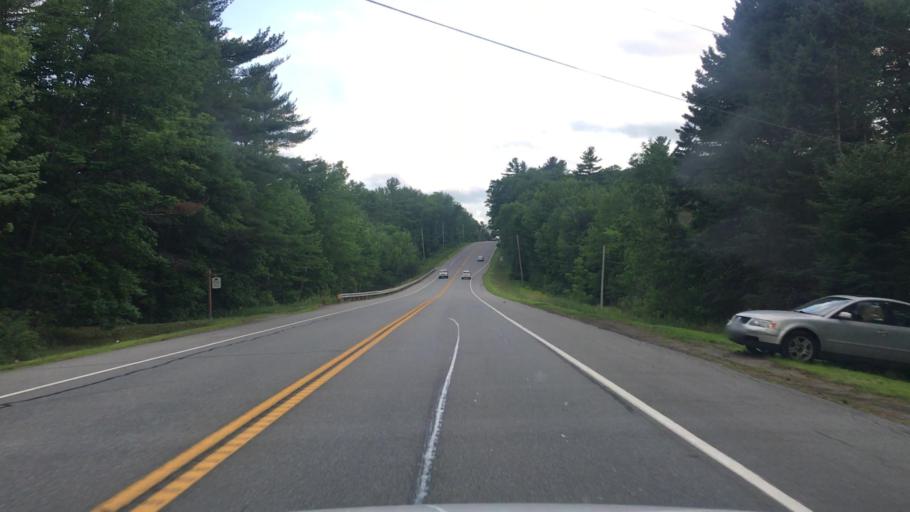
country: US
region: Maine
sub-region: Kennebec County
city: Windsor
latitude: 44.3795
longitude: -69.6208
